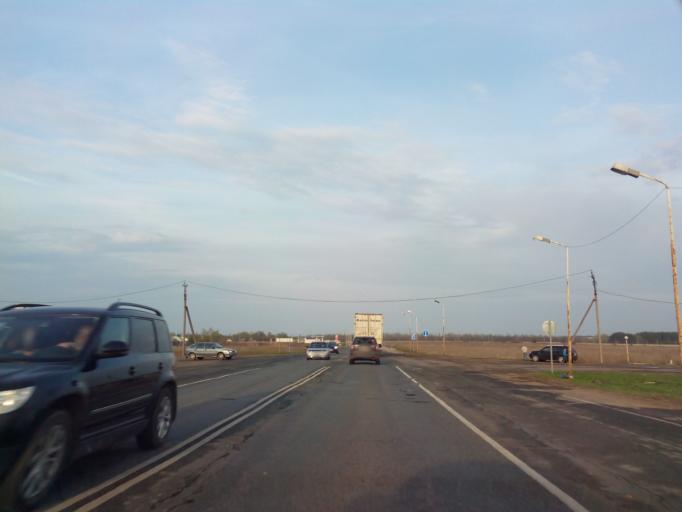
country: RU
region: Rjazan
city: Zarechnyy
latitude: 53.7521
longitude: 39.8084
